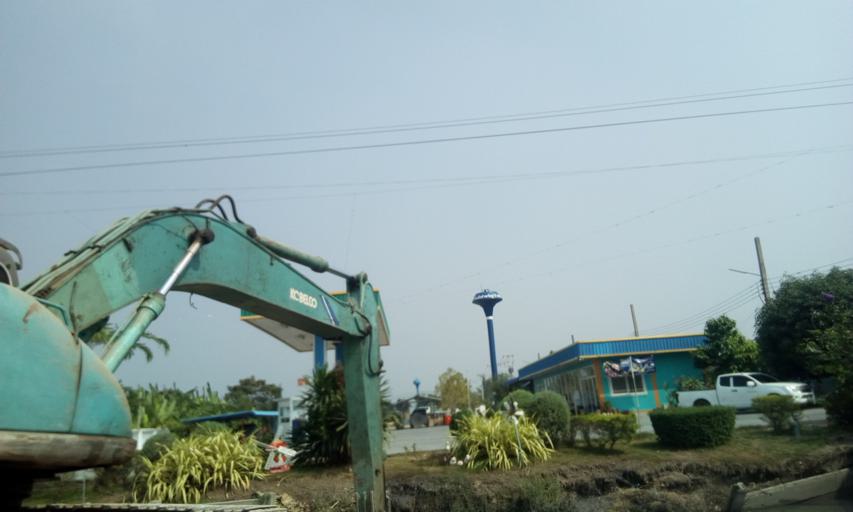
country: TH
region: Pathum Thani
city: Lam Luk Ka
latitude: 13.9628
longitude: 100.7254
